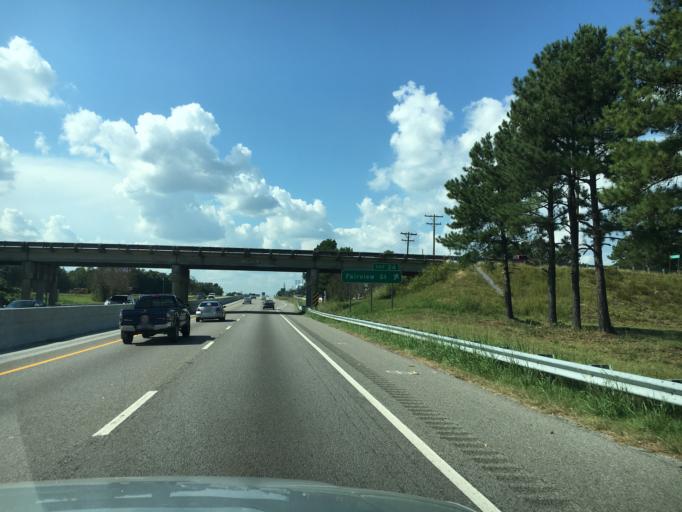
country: US
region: South Carolina
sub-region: Greenville County
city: Fountain Inn
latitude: 34.6880
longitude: -82.2169
